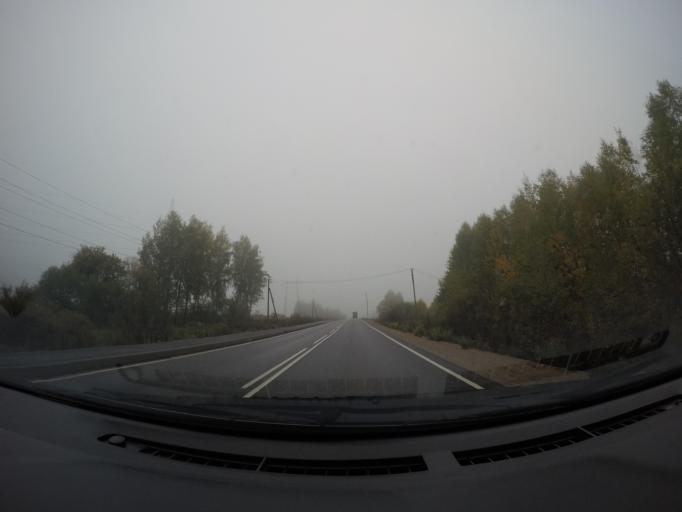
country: RU
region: Moskovskaya
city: Rumyantsevo
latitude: 55.8437
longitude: 36.4831
